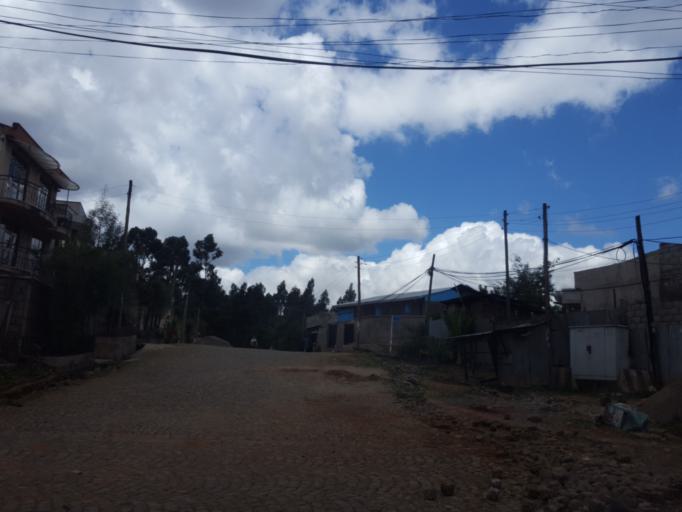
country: ET
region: Adis Abeba
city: Addis Ababa
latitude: 9.0660
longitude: 38.7303
